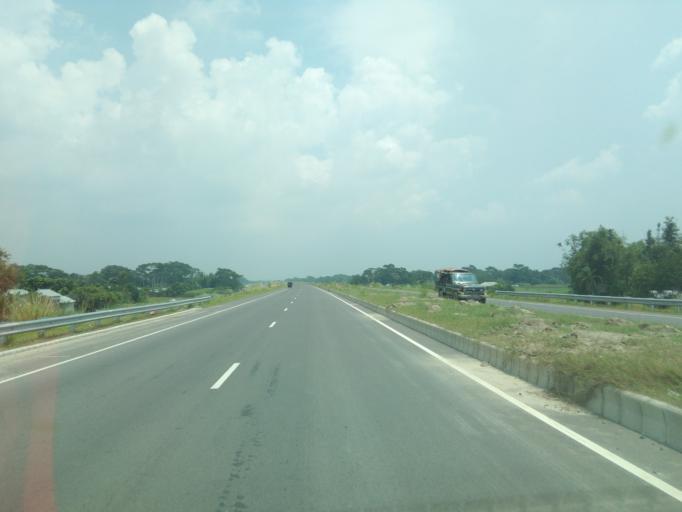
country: BD
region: Dhaka
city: Char Bhadrasan
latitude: 23.3991
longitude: 90.1878
